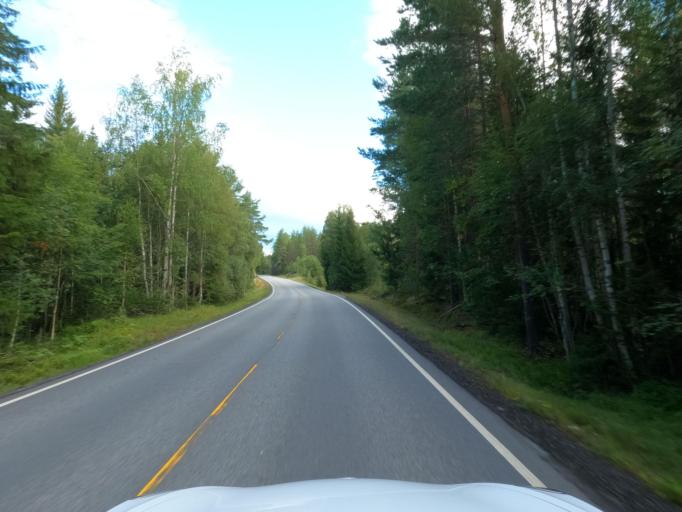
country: NO
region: Telemark
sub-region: Notodden
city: Notodden
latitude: 59.7302
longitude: 9.1596
